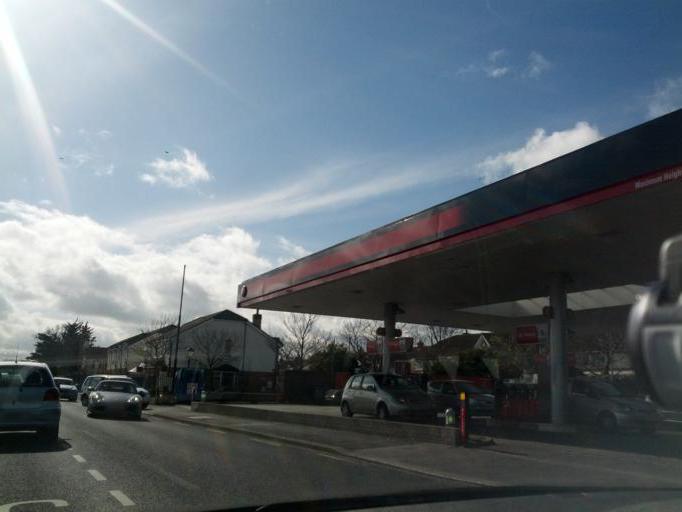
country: IE
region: Leinster
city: Portmarnock
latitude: 53.4196
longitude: -6.1397
